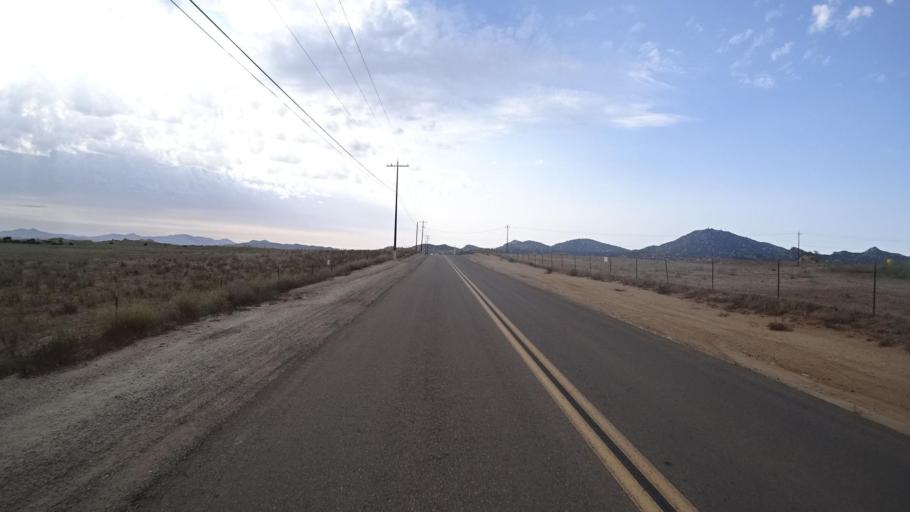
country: US
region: California
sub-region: San Diego County
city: San Pasqual
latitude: 33.0429
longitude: -116.9360
